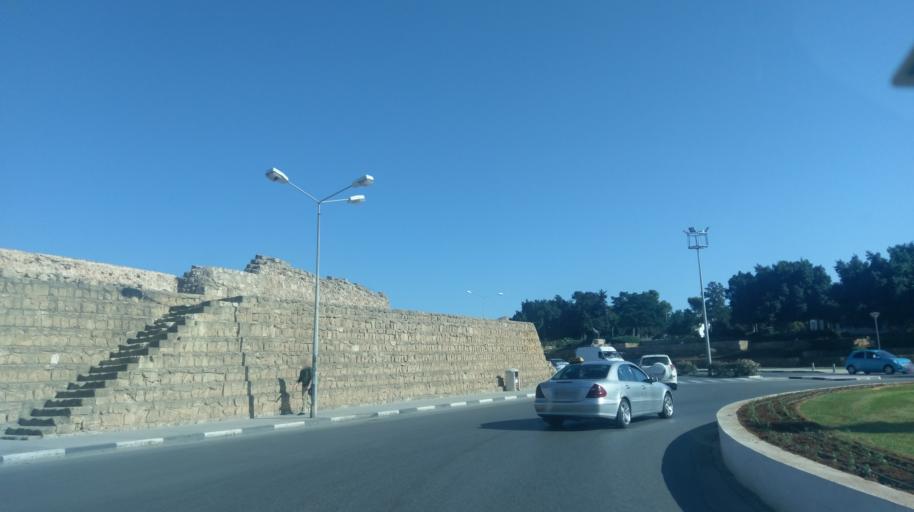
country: CY
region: Ammochostos
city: Famagusta
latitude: 35.1207
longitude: 33.9383
